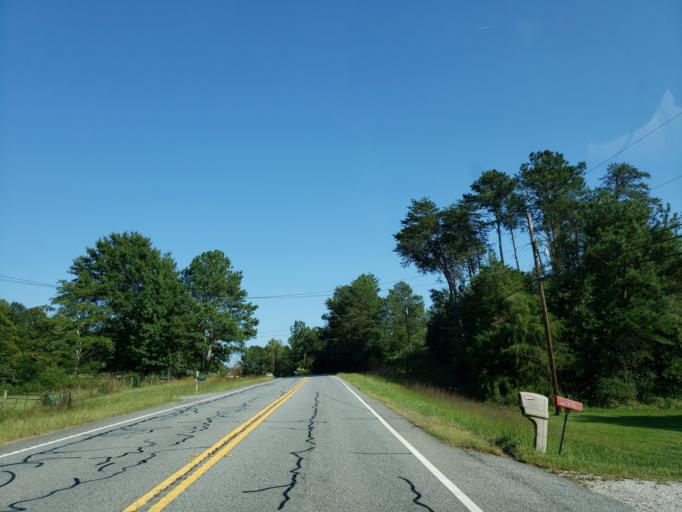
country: US
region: Georgia
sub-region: Catoosa County
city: Ringgold
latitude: 34.8995
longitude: -85.0498
